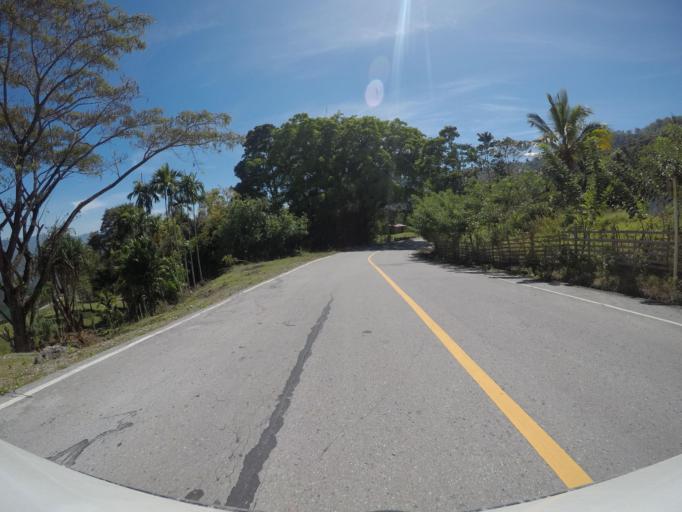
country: TL
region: Manufahi
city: Same
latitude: -8.9112
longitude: 125.9732
